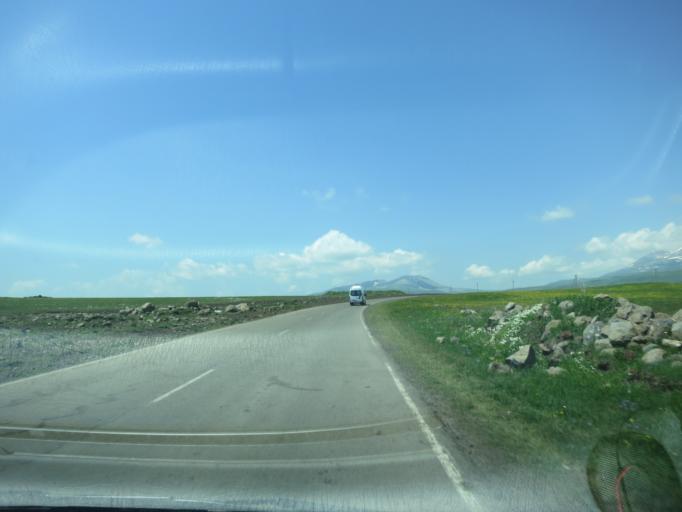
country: GE
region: Samtskhe-Javakheti
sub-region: Ninotsminda
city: Ninotsminda
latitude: 41.4057
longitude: 43.8139
